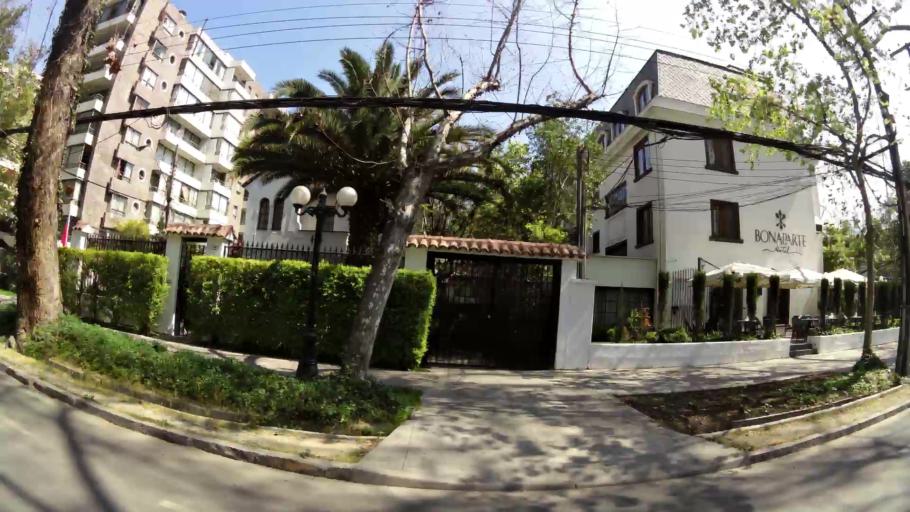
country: CL
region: Santiago Metropolitan
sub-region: Provincia de Santiago
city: Villa Presidente Frei, Nunoa, Santiago, Chile
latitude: -33.4326
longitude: -70.6058
